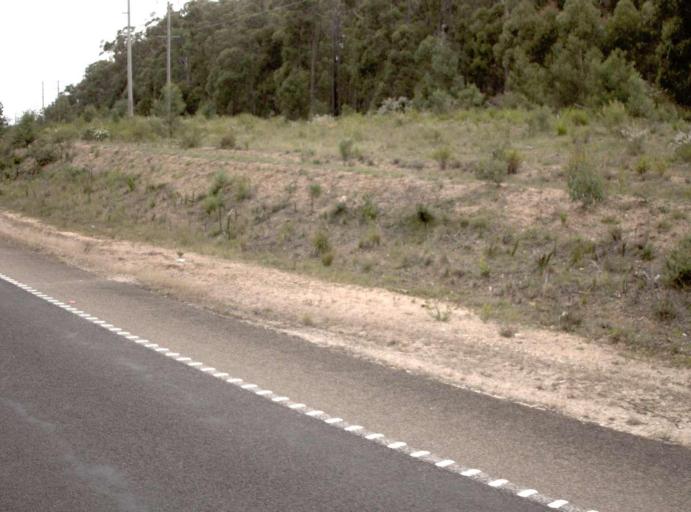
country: AU
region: Victoria
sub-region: East Gippsland
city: Lakes Entrance
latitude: -37.7066
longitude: 148.0680
